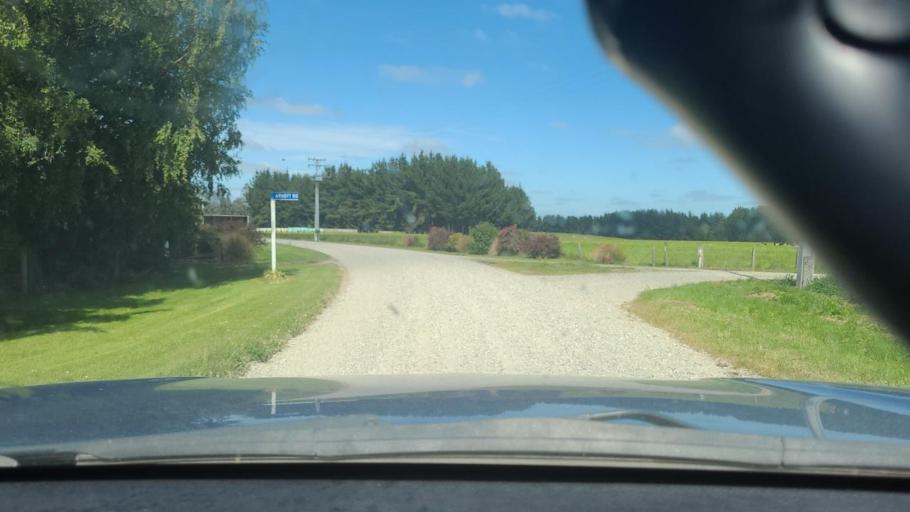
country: NZ
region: Southland
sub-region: Gore District
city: Gore
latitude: -46.3106
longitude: 168.8852
